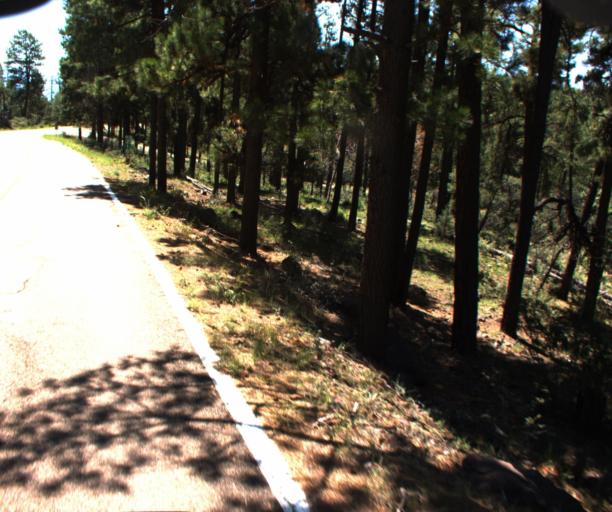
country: US
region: Arizona
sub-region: Greenlee County
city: Morenci
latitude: 33.5222
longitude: -109.3071
